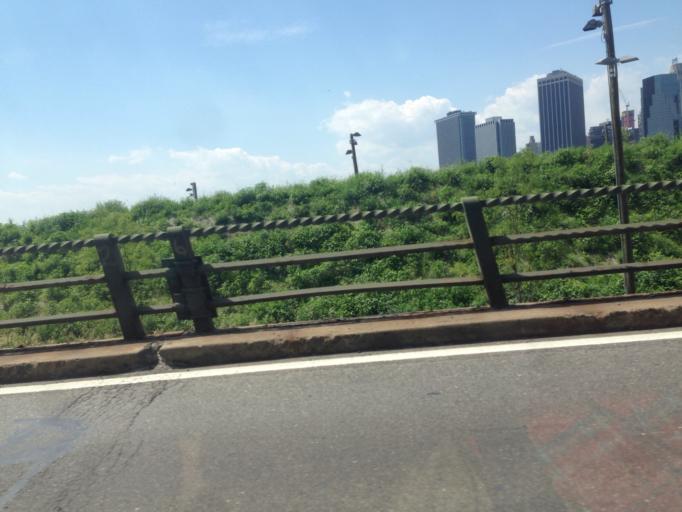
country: US
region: New York
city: New York City
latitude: 40.6970
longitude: -73.9977
